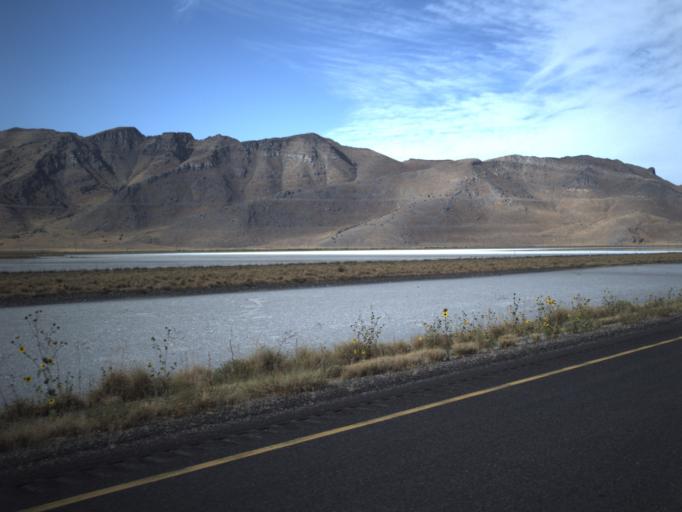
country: US
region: Utah
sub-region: Tooele County
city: Grantsville
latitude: 40.7276
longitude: -112.5790
